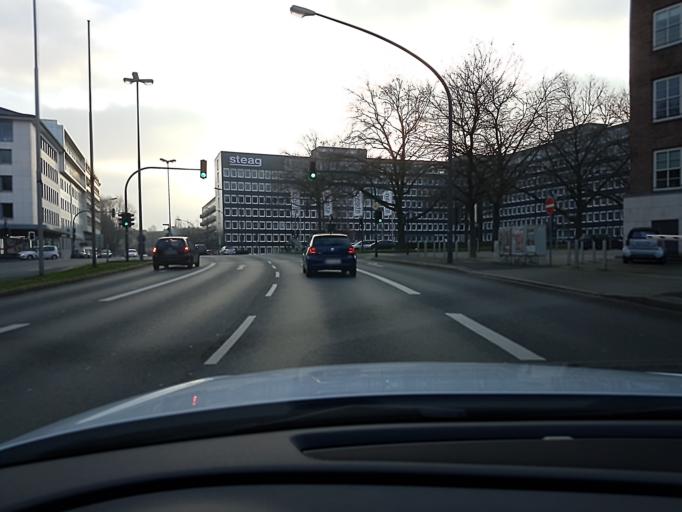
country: DE
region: North Rhine-Westphalia
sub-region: Regierungsbezirk Dusseldorf
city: Essen
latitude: 51.4440
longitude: 7.0070
